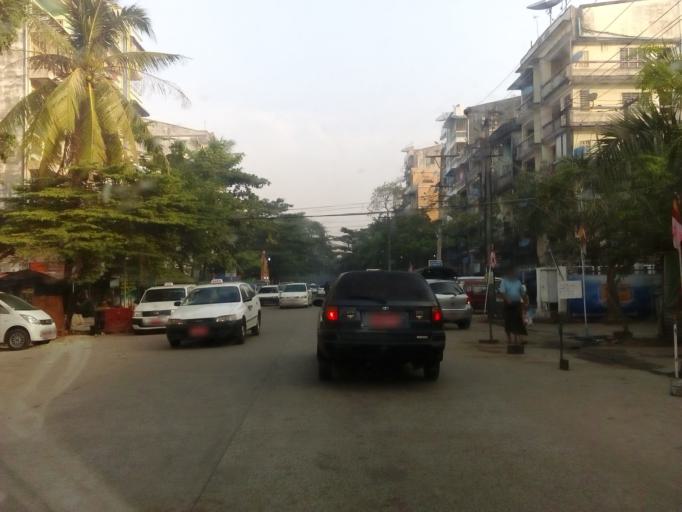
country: MM
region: Yangon
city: Yangon
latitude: 16.8031
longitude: 96.1789
